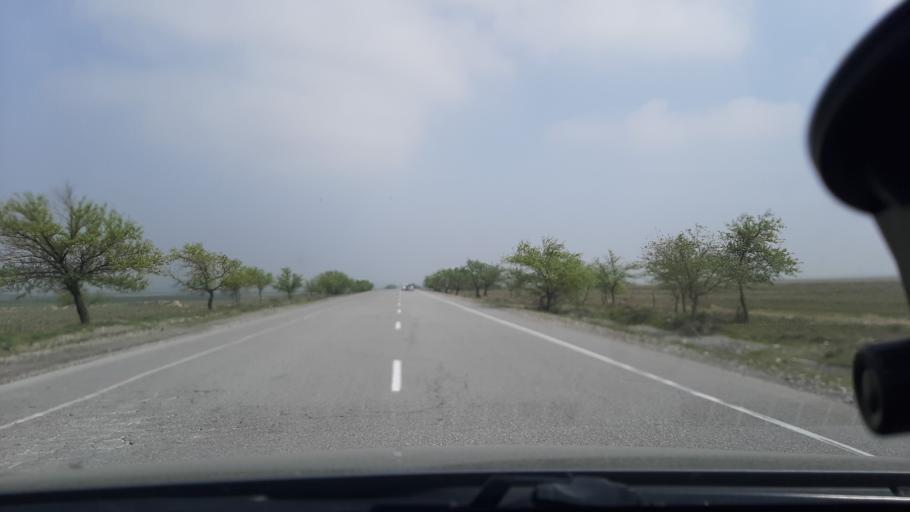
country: UZ
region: Toshkent
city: Bekobod
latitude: 40.1056
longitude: 69.1831
